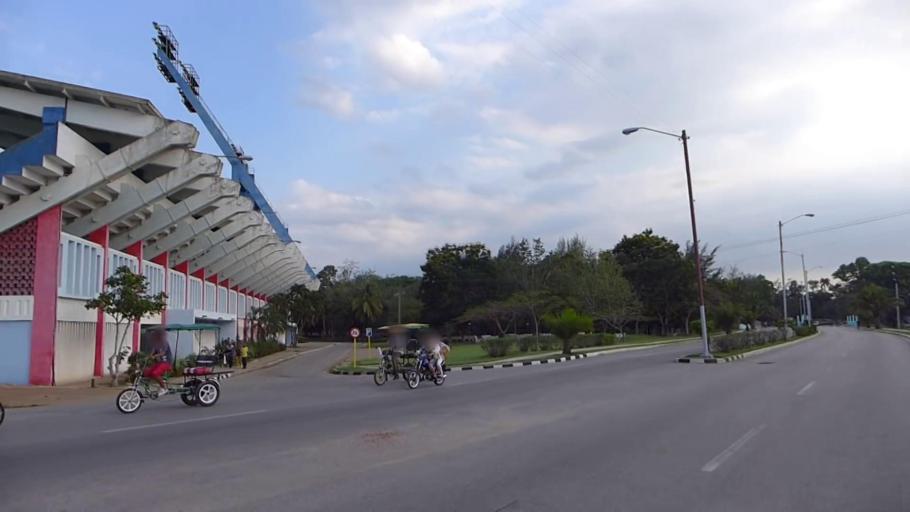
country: CU
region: Camaguey
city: Camaguey
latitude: 21.3794
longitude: -77.9120
